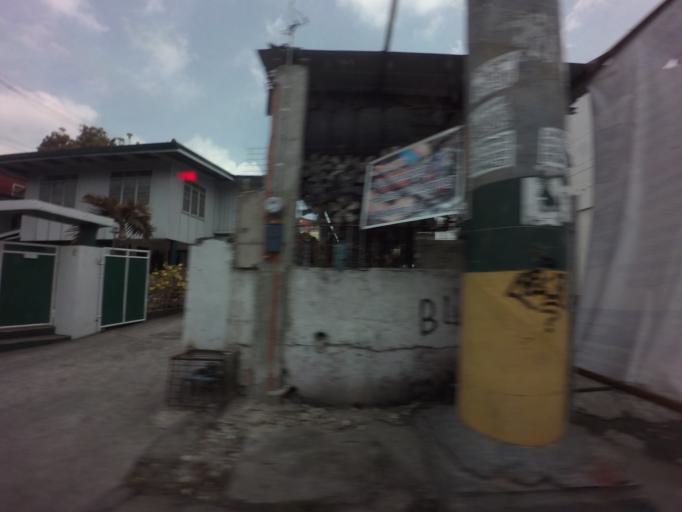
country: PH
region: Calabarzon
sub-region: Province of Rizal
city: Taguig
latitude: 14.4749
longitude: 121.0594
